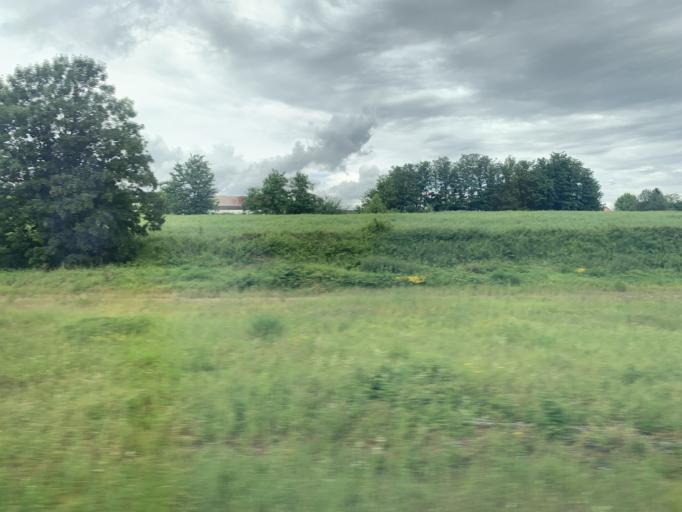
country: FR
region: Alsace
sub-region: Departement du Haut-Rhin
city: Dannemarie
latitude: 47.6281
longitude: 7.1274
